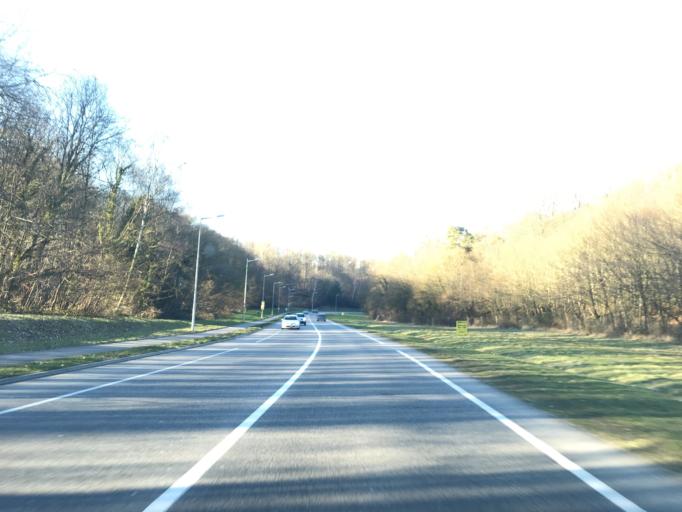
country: FR
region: Haute-Normandie
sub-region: Departement de l'Eure
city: Evreux
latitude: 49.0091
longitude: 1.1433
